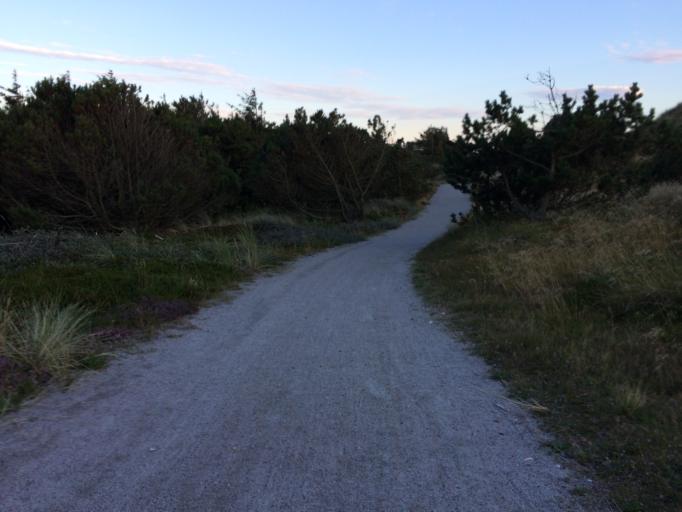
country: DK
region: Central Jutland
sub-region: Ringkobing-Skjern Kommune
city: Hvide Sande
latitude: 55.8748
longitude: 8.1710
